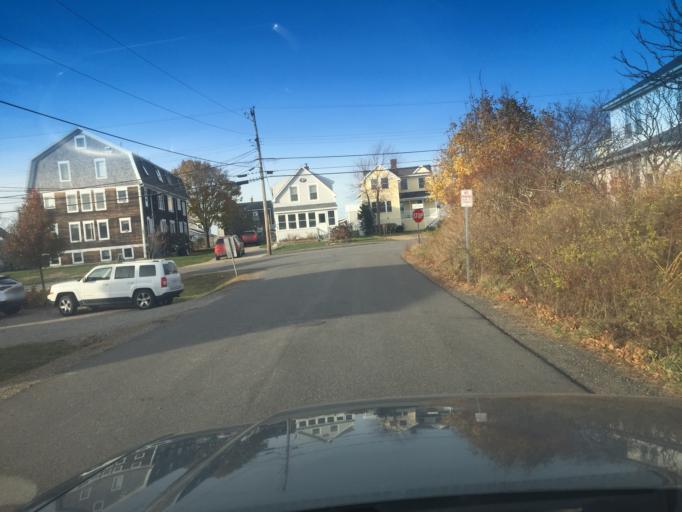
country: US
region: Maine
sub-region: York County
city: York Beach
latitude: 43.1720
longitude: -70.6048
